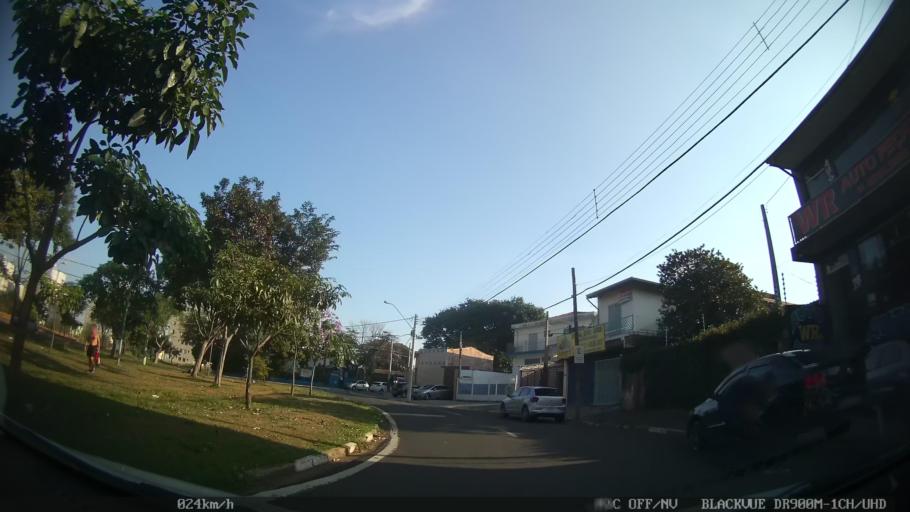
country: BR
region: Sao Paulo
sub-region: Campinas
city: Campinas
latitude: -22.9714
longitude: -47.1390
